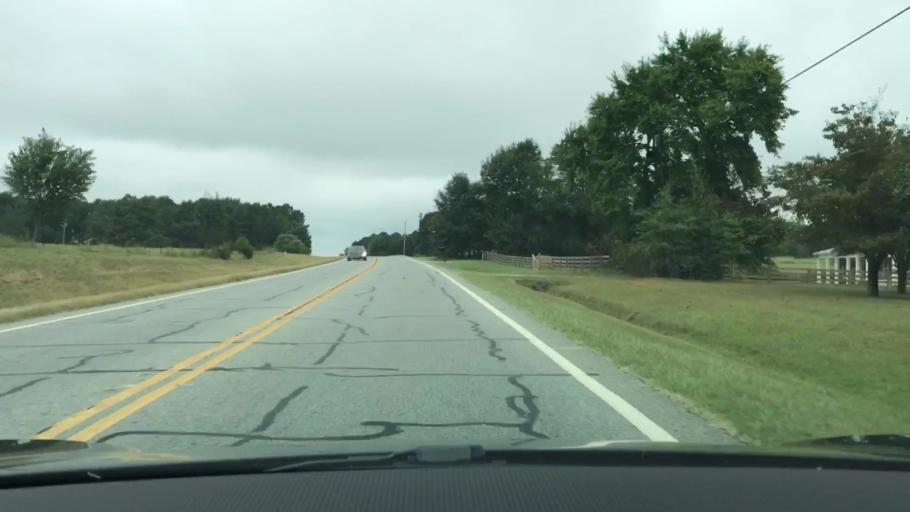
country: US
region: Georgia
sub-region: Oconee County
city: Watkinsville
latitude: 33.8428
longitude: -83.3877
